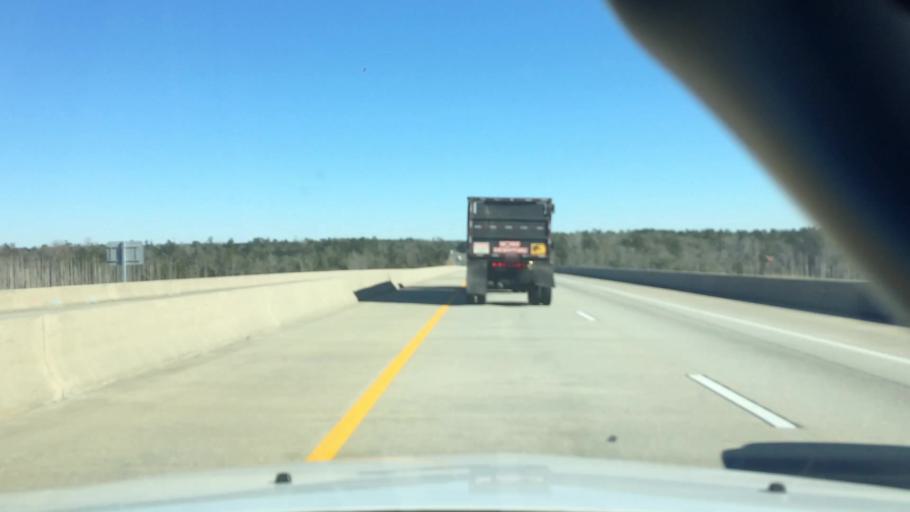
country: US
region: North Carolina
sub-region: New Hanover County
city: Wrightsboro
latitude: 34.3018
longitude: -77.9568
